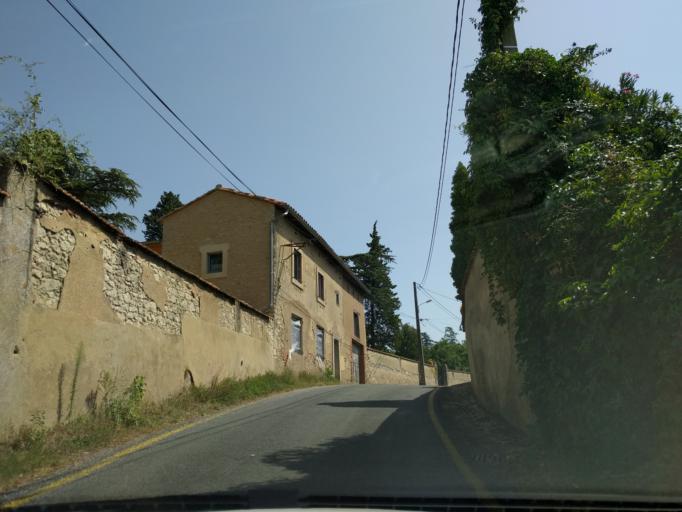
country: FR
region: Midi-Pyrenees
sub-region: Departement du Tarn
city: Castres
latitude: 43.6001
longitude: 2.2473
